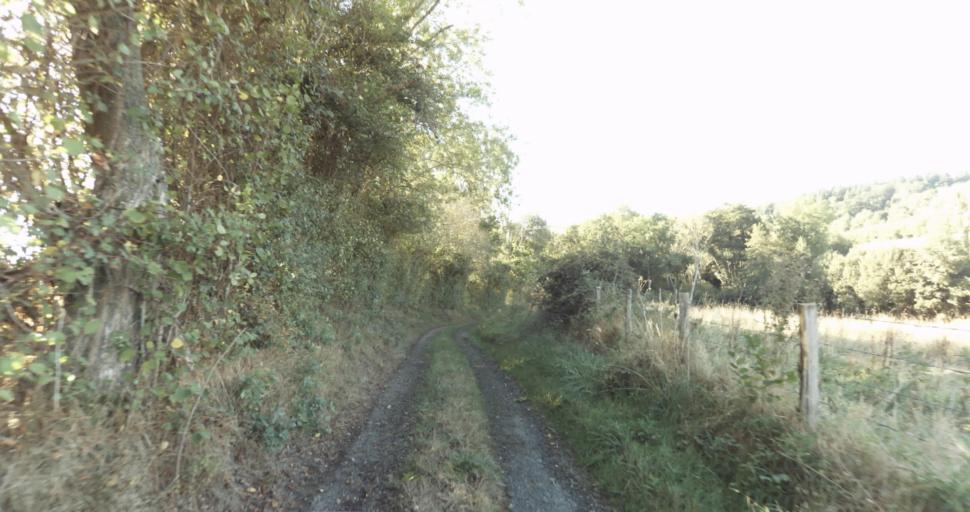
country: FR
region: Lower Normandy
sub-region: Departement de l'Orne
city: Vimoutiers
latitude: 48.8817
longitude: 0.1176
